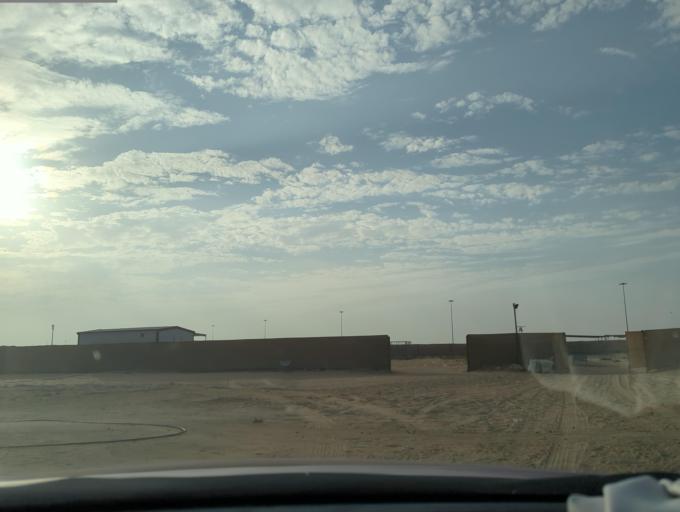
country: AE
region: Dubai
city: Dubai
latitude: 24.7194
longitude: 54.8670
